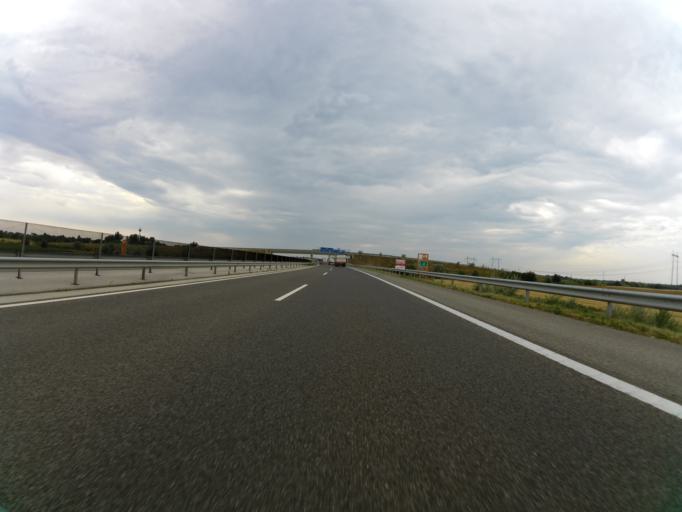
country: HU
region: Csongrad
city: Sandorfalva
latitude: 46.2960
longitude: 20.0929
